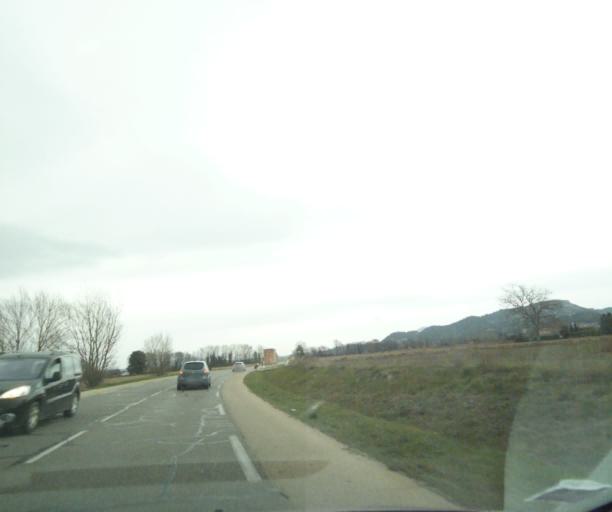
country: FR
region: Provence-Alpes-Cote d'Azur
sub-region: Departement des Bouches-du-Rhone
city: Meyrargues
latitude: 43.6522
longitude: 5.5172
